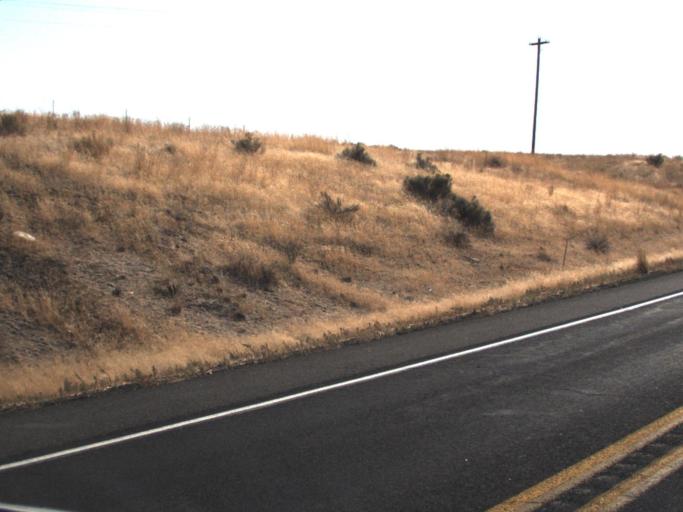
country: US
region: Washington
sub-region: Franklin County
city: Basin City
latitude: 46.5721
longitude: -119.0036
